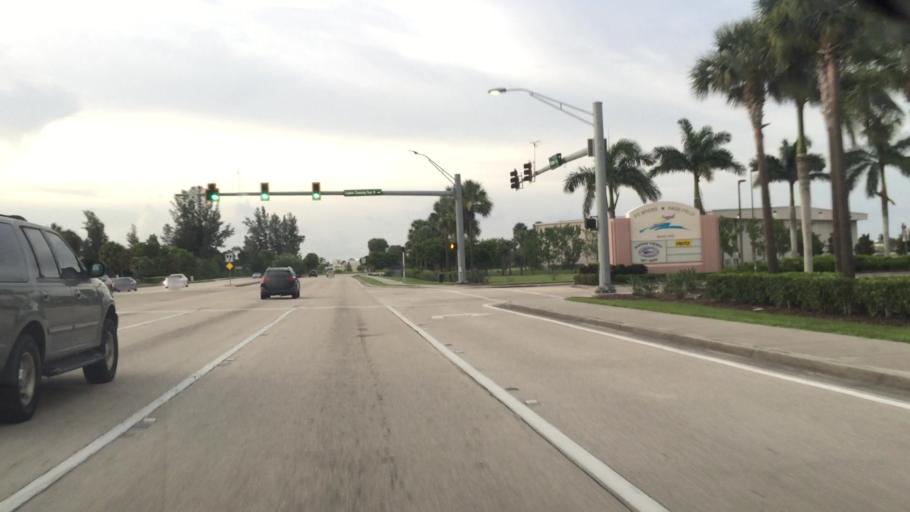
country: US
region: Florida
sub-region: Lee County
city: Pine Manor
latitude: 26.5880
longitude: -81.8687
